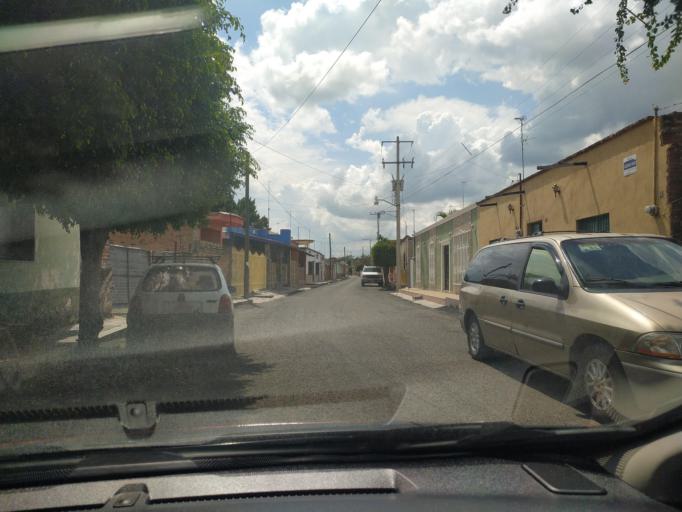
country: MX
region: Jalisco
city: Villa Corona
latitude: 20.3494
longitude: -103.6747
